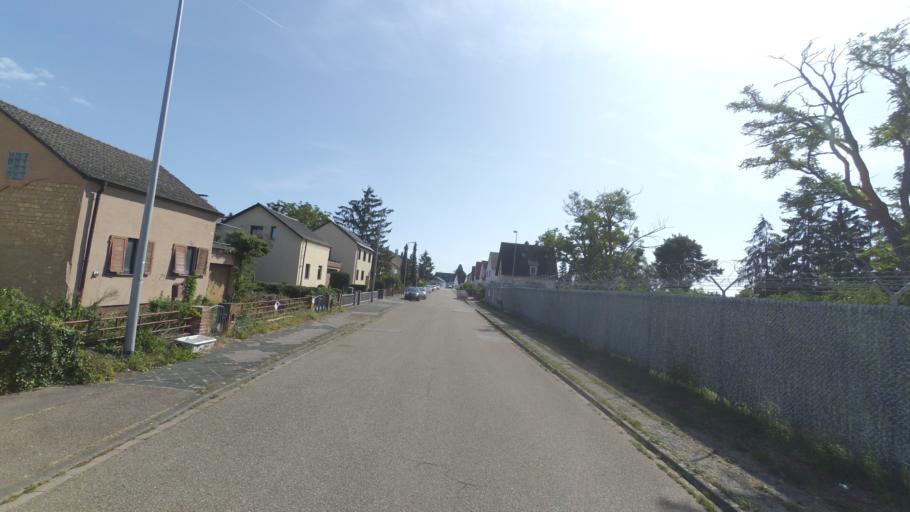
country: DE
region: Hesse
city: Lampertheim
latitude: 49.5635
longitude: 8.4786
